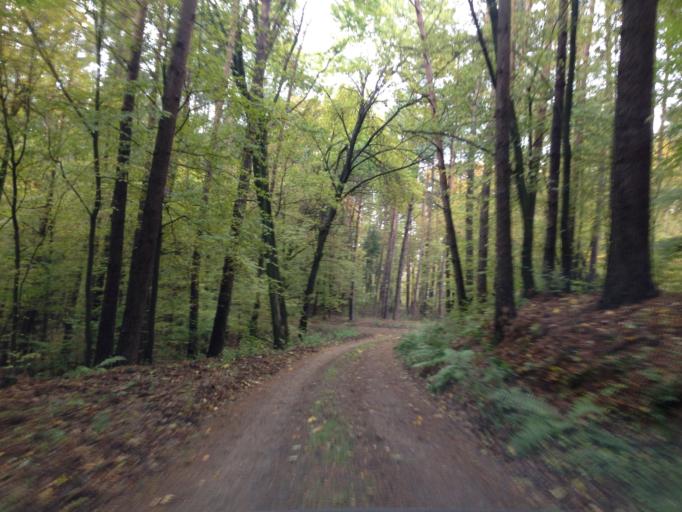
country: PL
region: Kujawsko-Pomorskie
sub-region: Powiat brodnicki
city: Gorzno
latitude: 53.2627
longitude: 19.7011
